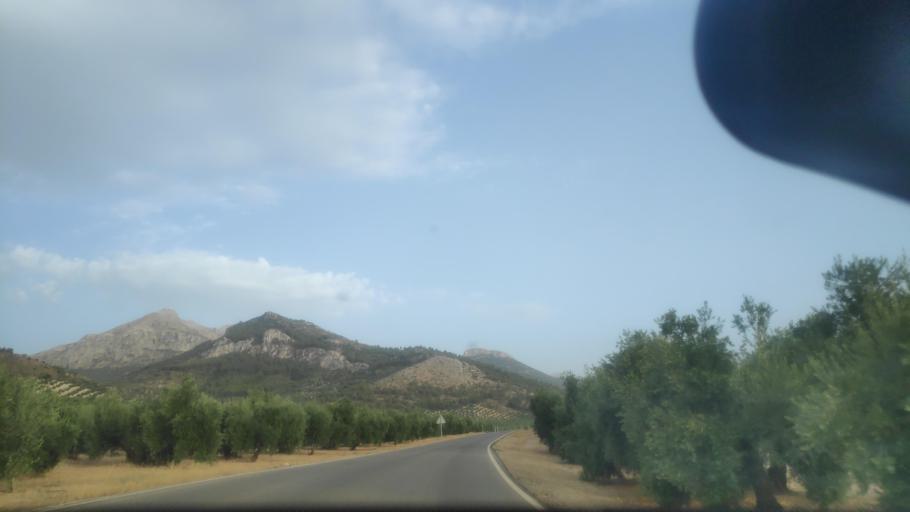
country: ES
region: Andalusia
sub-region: Provincia de Jaen
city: Jimena
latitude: 37.8348
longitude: -3.5287
